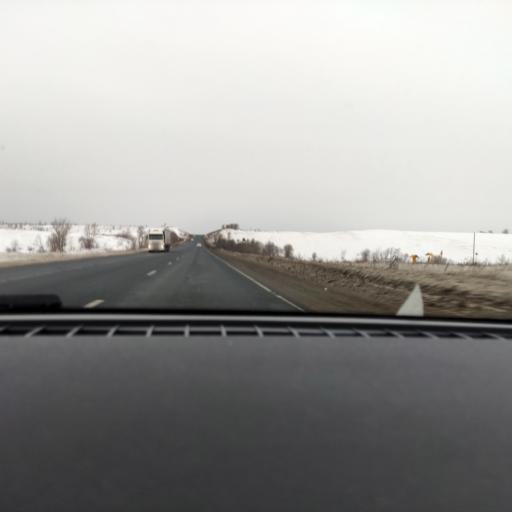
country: RU
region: Samara
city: Novosemeykino
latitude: 53.4039
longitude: 50.3839
